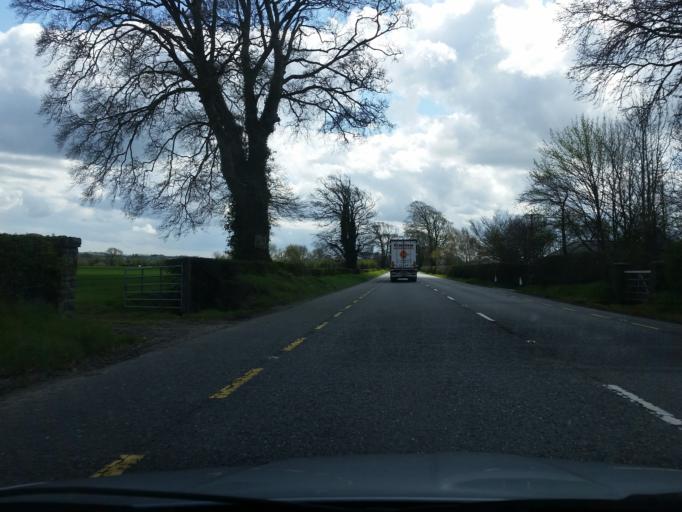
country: IE
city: Kentstown
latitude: 53.6089
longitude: -6.4761
